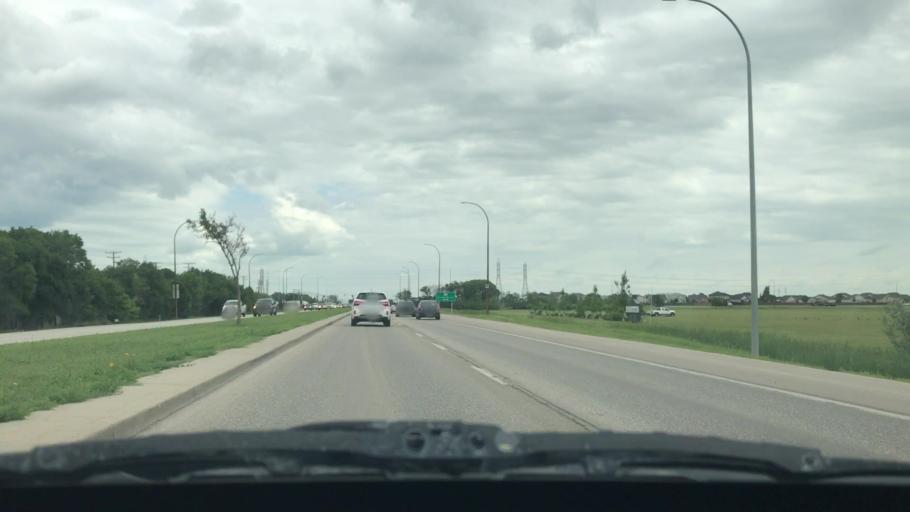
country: CA
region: Manitoba
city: Winnipeg
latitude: 49.8559
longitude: -97.0557
